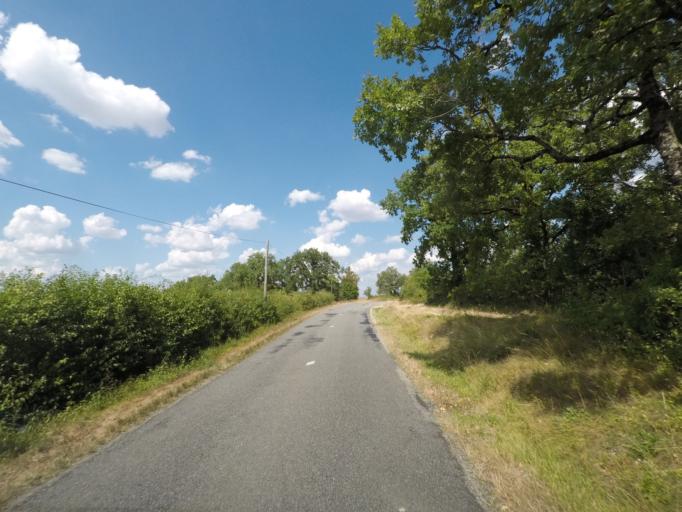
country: FR
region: Midi-Pyrenees
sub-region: Departement du Lot
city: Le Vigan
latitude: 44.6134
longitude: 1.5923
